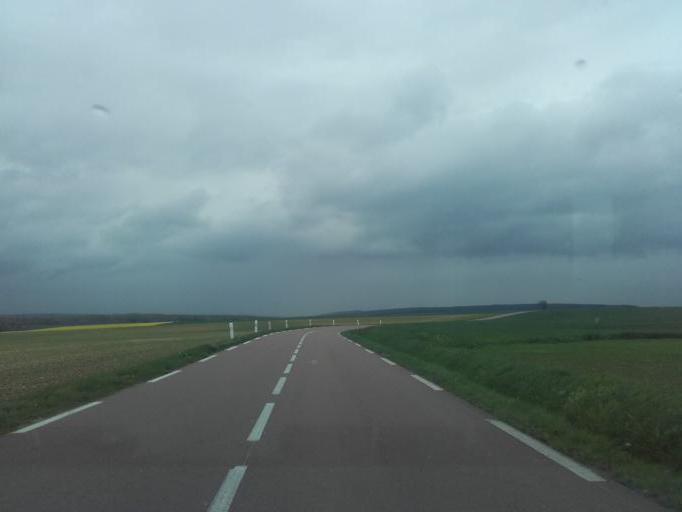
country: FR
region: Bourgogne
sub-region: Departement de l'Yonne
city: Joux-la-Ville
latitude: 47.7116
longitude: 3.8532
